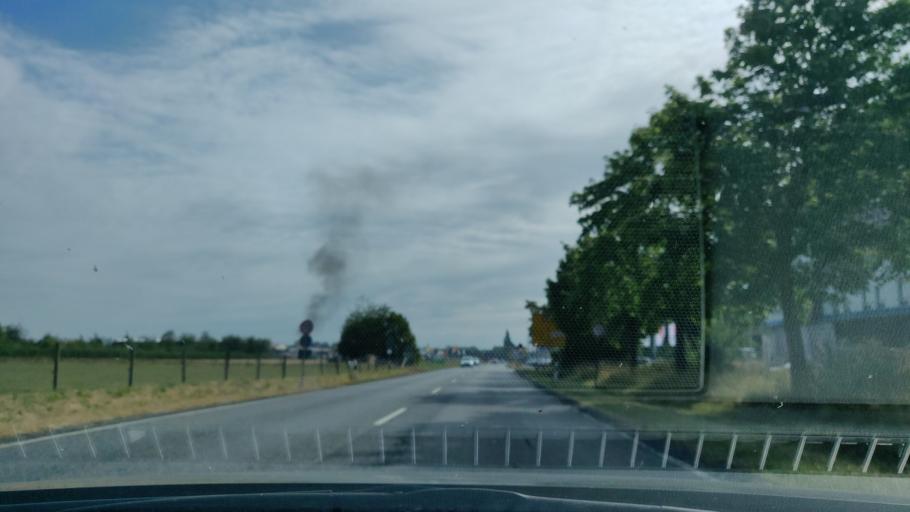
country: DE
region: Hesse
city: Fritzlar
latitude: 51.1394
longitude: 9.2705
